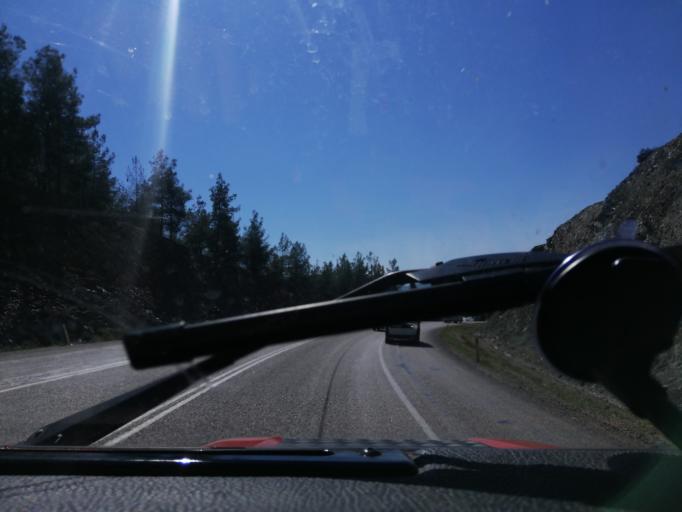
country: TR
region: Mugla
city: Kemer
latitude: 36.6090
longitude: 29.3585
